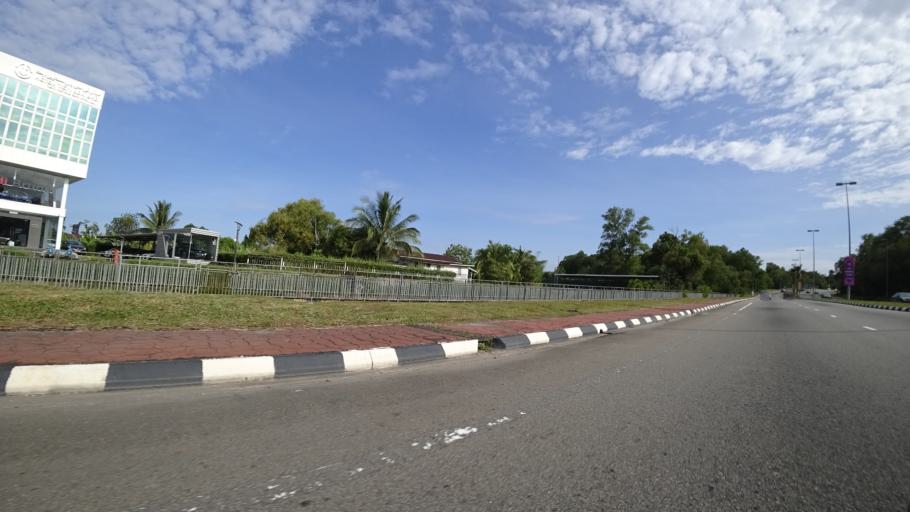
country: BN
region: Brunei and Muara
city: Bandar Seri Begawan
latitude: 4.8982
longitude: 114.9155
